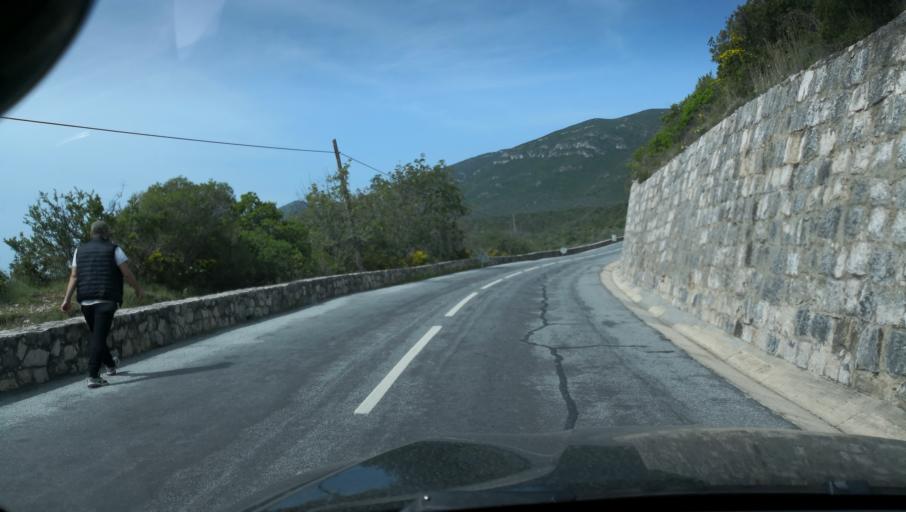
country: PT
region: Setubal
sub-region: Palmela
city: Quinta do Anjo
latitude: 38.4848
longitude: -8.9658
